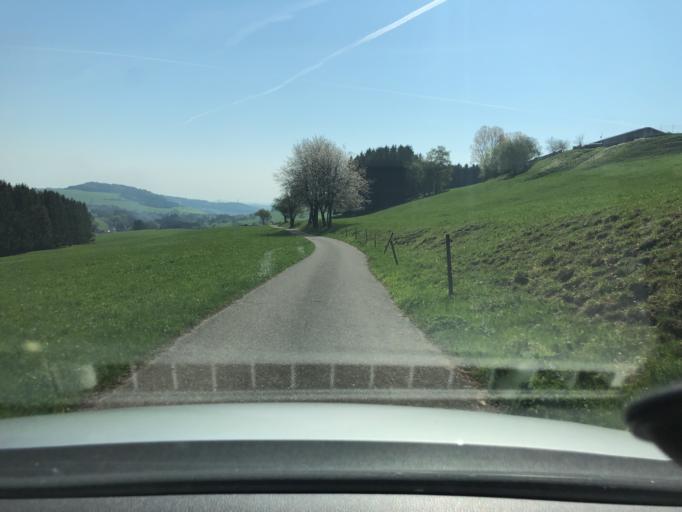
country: DE
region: Baden-Wuerttemberg
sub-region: Freiburg Region
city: Hochenschwand
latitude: 47.6727
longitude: 8.1634
